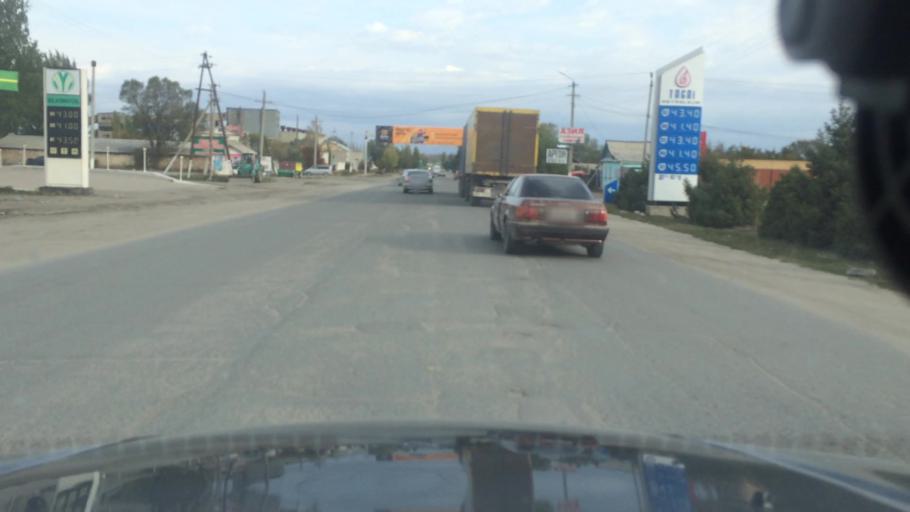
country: KG
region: Ysyk-Koel
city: Karakol
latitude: 42.5124
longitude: 78.3857
